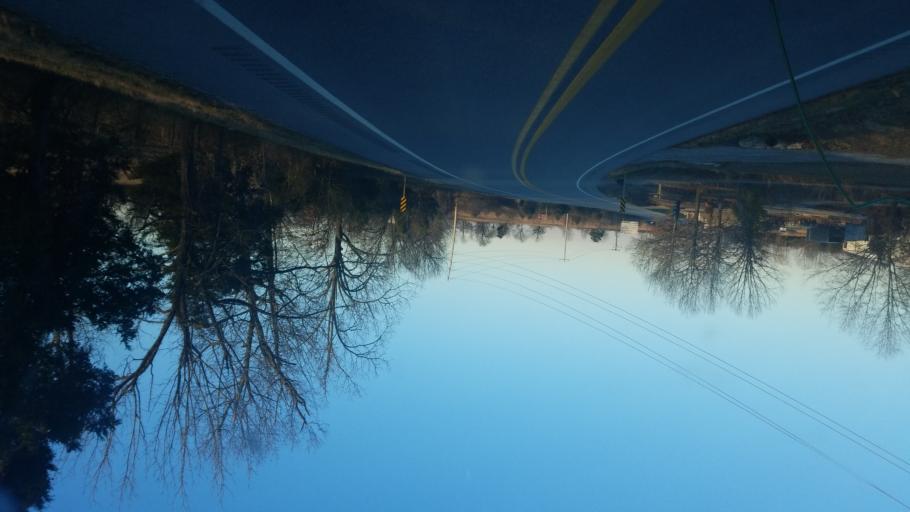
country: US
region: Arkansas
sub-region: Baxter County
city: Mountain Home
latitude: 36.3759
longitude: -92.1495
